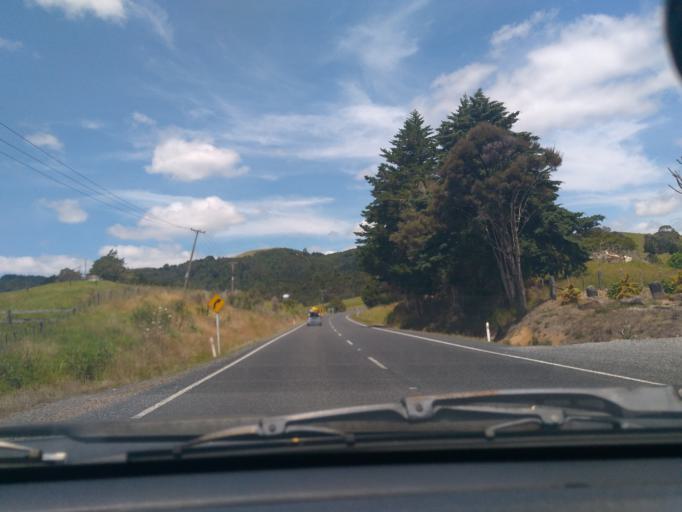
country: NZ
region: Northland
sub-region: Far North District
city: Kerikeri
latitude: -35.1138
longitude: 173.8128
